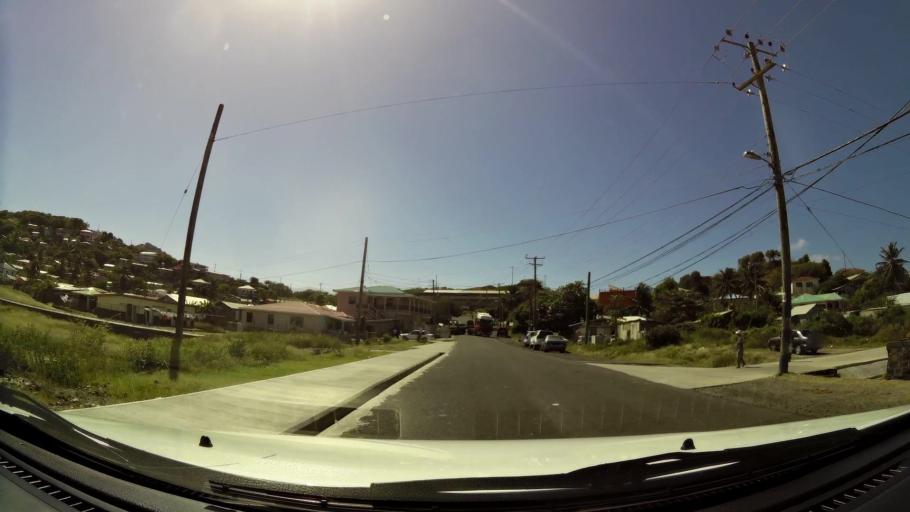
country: LC
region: Vieux-Fort
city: Vieux Fort
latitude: 13.7265
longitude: -60.9524
